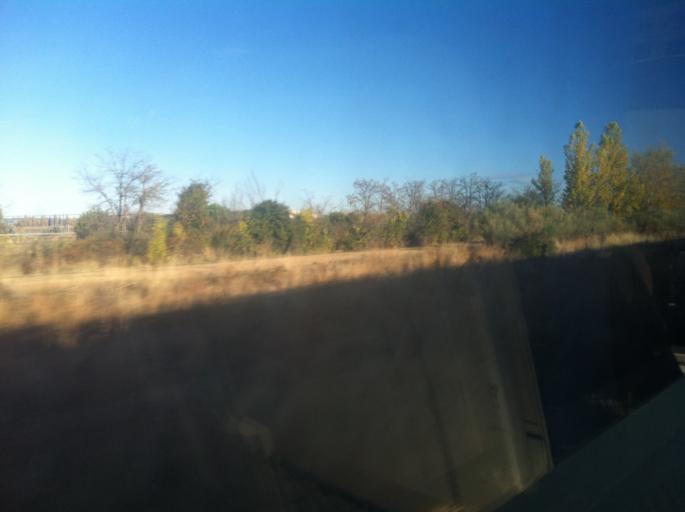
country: ES
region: Castille and Leon
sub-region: Provincia de Valladolid
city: Cabezon
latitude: 41.7570
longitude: -4.6320
